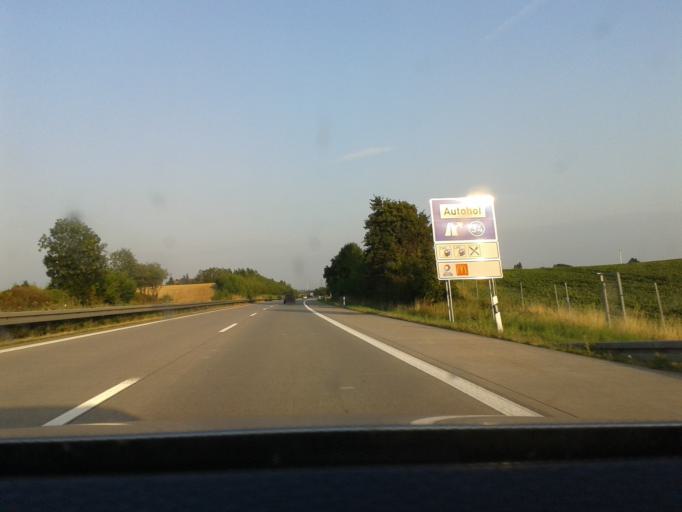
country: DE
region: Saxony
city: Grossweitzschen
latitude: 51.1650
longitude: 13.0932
